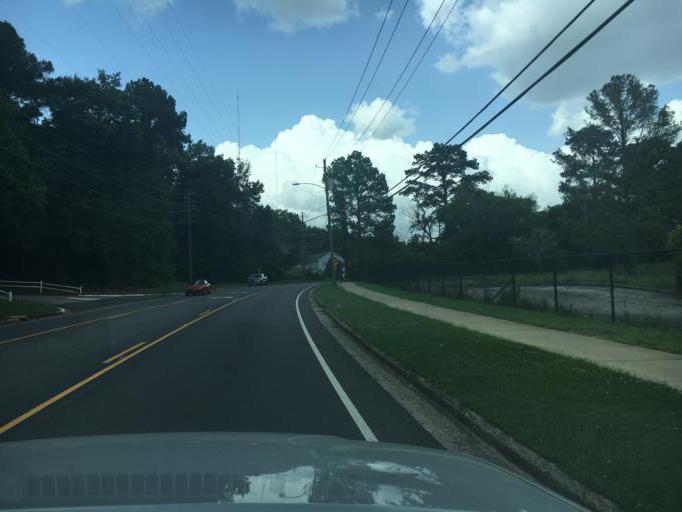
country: US
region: Alabama
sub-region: Jefferson County
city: Homewood
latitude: 33.4816
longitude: -86.8062
